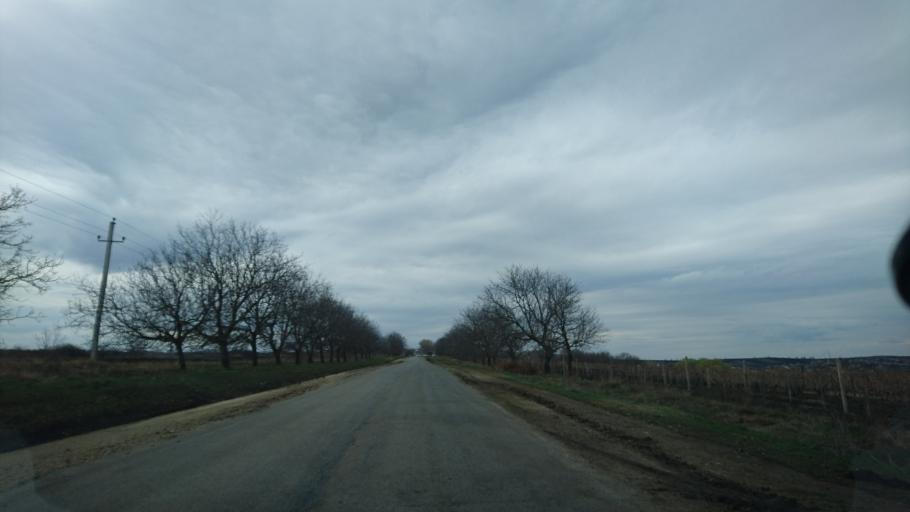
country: MD
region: Cantemir
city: Visniovca
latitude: 46.3462
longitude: 28.4198
